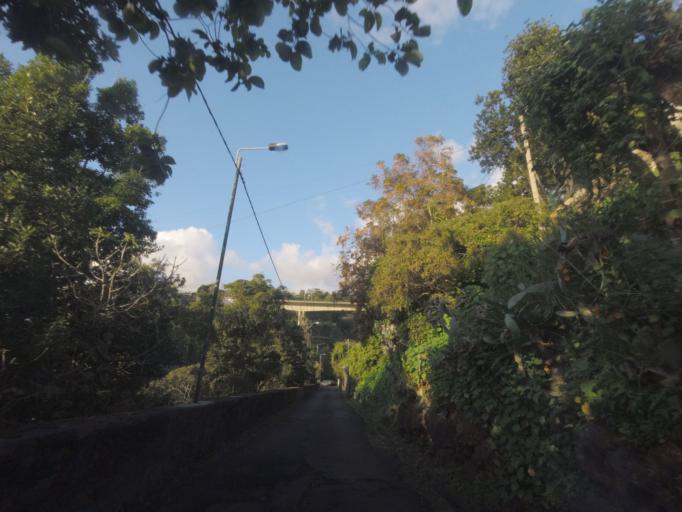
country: PT
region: Madeira
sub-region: Funchal
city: Nossa Senhora do Monte
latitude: 32.6535
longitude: -16.8811
